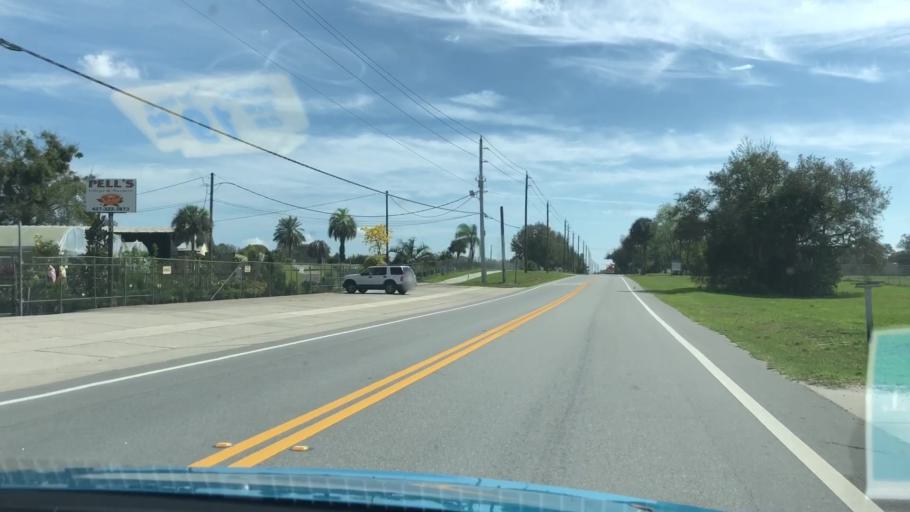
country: US
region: Florida
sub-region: Seminole County
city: Midway
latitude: 28.8526
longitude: -81.1736
